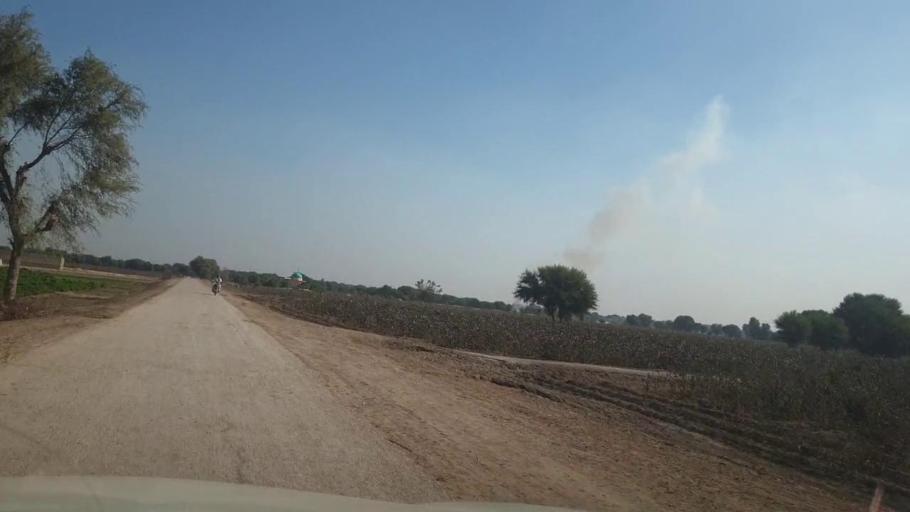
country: PK
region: Sindh
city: Bhan
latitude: 26.5793
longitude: 67.7017
